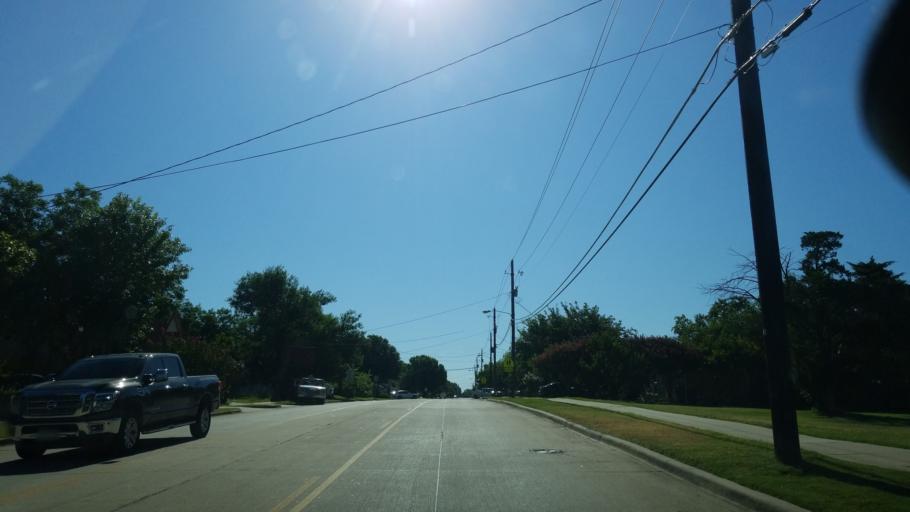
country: US
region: Texas
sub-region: Dallas County
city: Carrollton
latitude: 32.9492
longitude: -96.8989
